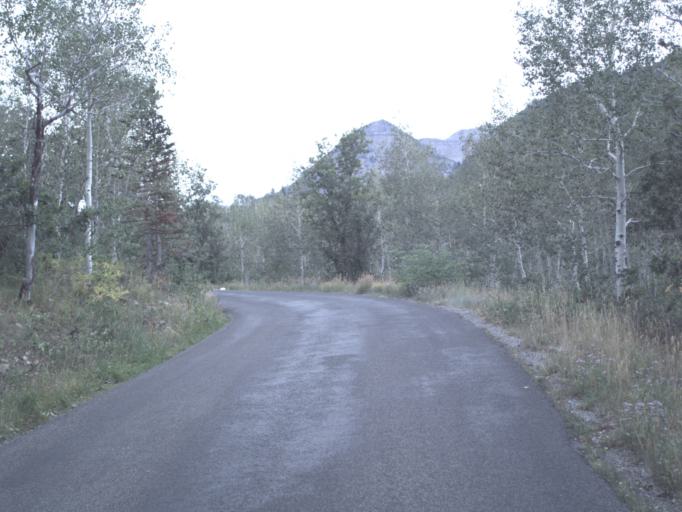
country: US
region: Utah
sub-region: Utah County
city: Lindon
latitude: 40.4331
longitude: -111.6153
